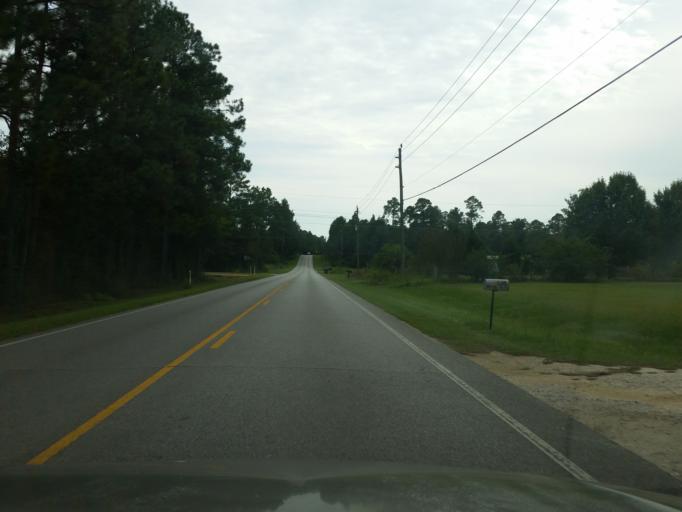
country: US
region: Florida
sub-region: Escambia County
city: Molino
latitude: 30.6713
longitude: -87.3199
